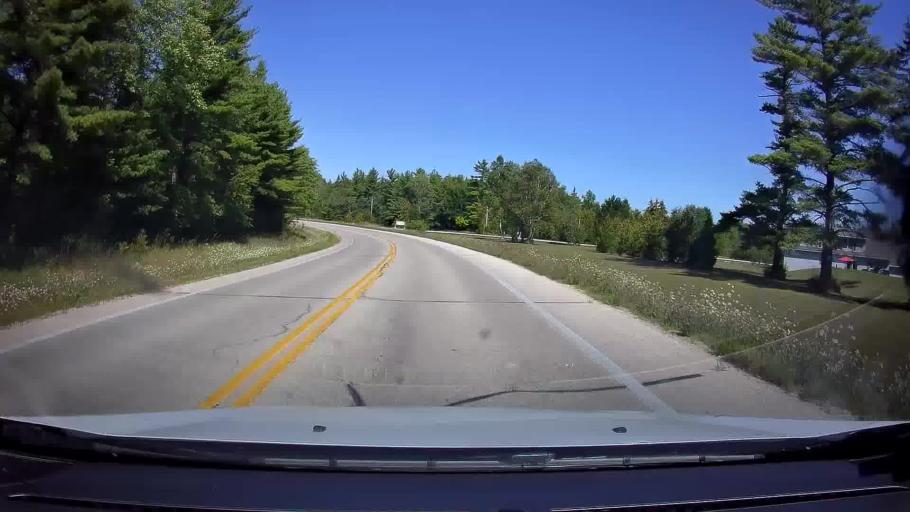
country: US
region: Michigan
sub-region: Delta County
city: Escanaba
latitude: 45.2605
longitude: -87.0214
